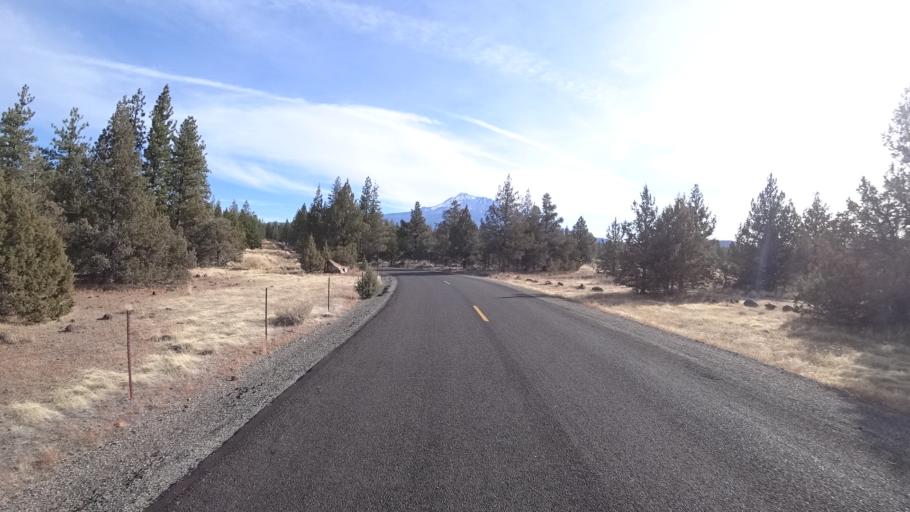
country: US
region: California
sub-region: Siskiyou County
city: Weed
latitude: 41.4981
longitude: -122.3887
